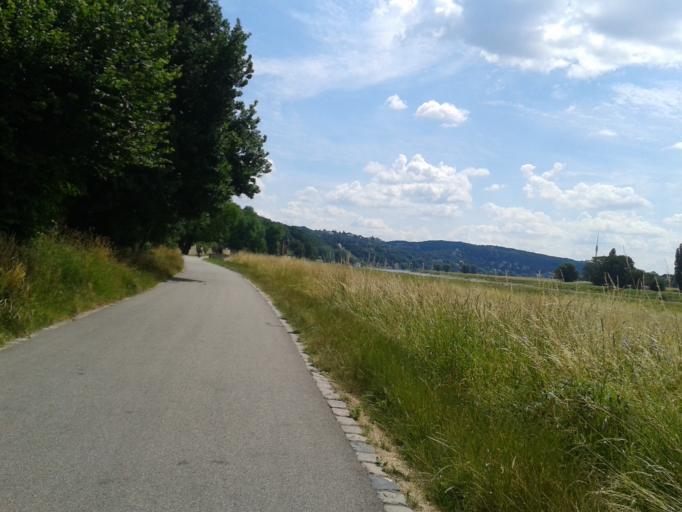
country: DE
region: Saxony
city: Albertstadt
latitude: 51.0656
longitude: 13.7796
